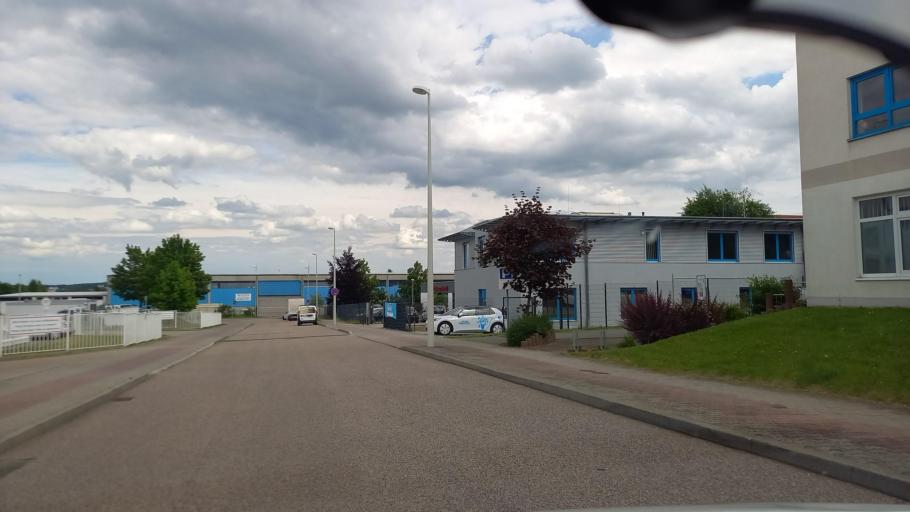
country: DE
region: Saxony
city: Weissenborn
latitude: 50.7245
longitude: 12.4720
